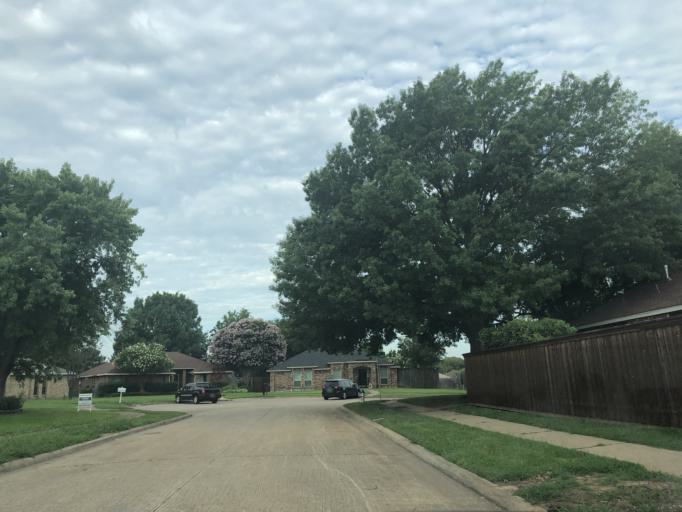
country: US
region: Texas
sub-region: Dallas County
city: Sunnyvale
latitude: 32.8410
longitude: -96.5633
